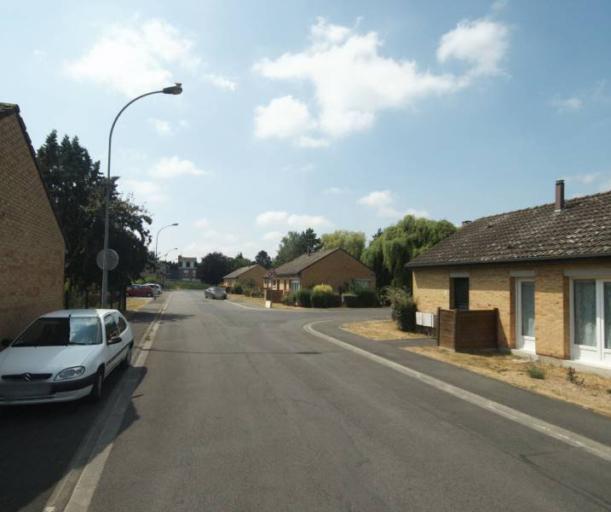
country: FR
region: Nord-Pas-de-Calais
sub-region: Departement du Nord
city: Armentieres
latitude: 50.6935
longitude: 2.8956
